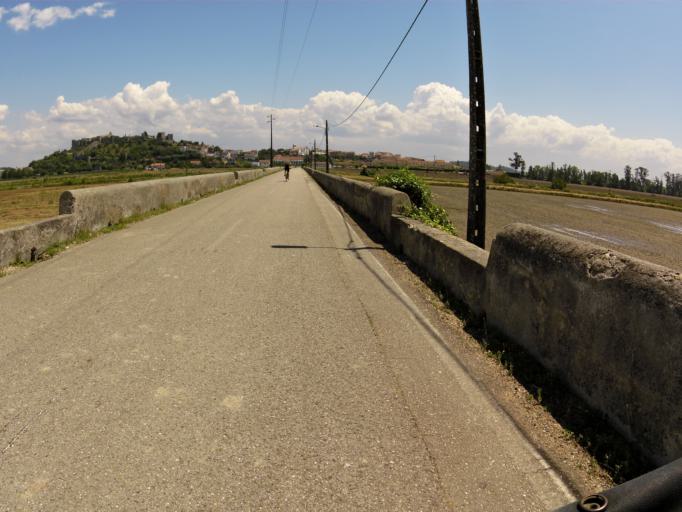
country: PT
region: Coimbra
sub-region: Montemor-O-Velho
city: Montemor-o-Velho
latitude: 40.1763
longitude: -8.6936
